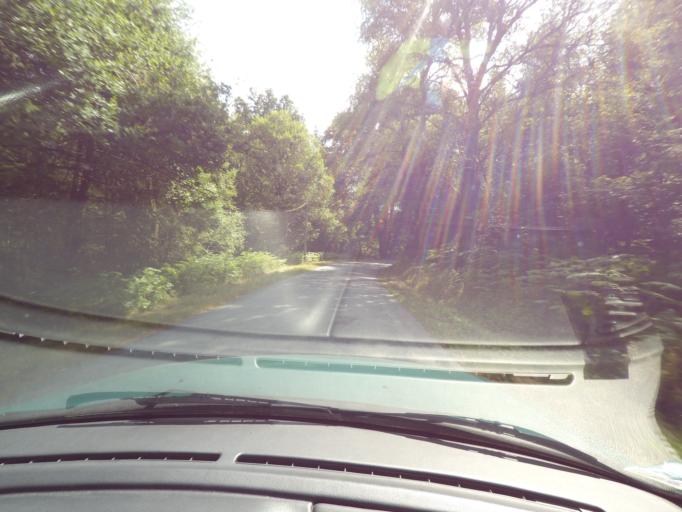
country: FR
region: Limousin
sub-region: Departement de la Correze
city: Bugeat
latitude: 45.7509
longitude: 1.9563
